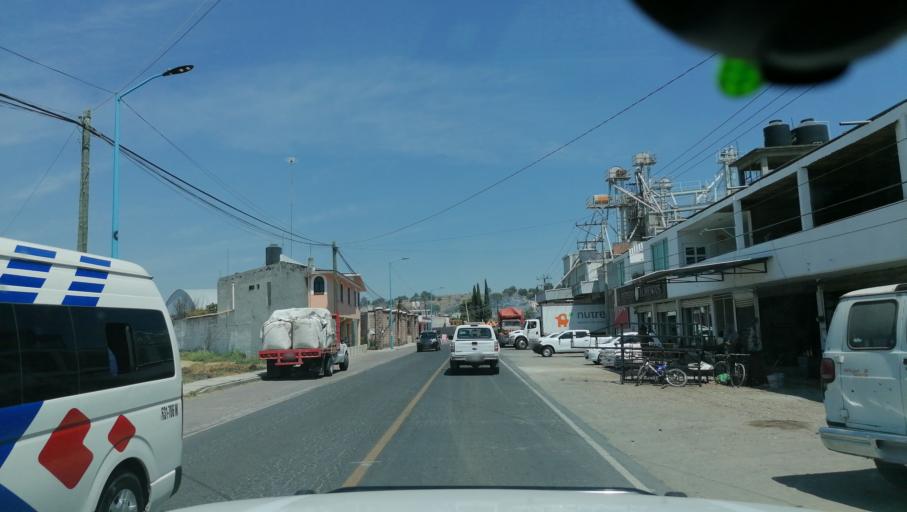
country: MX
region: Tlaxcala
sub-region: Tetlatlahuca
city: Santa Cruz Aquiahuac
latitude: 19.2356
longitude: -98.2836
